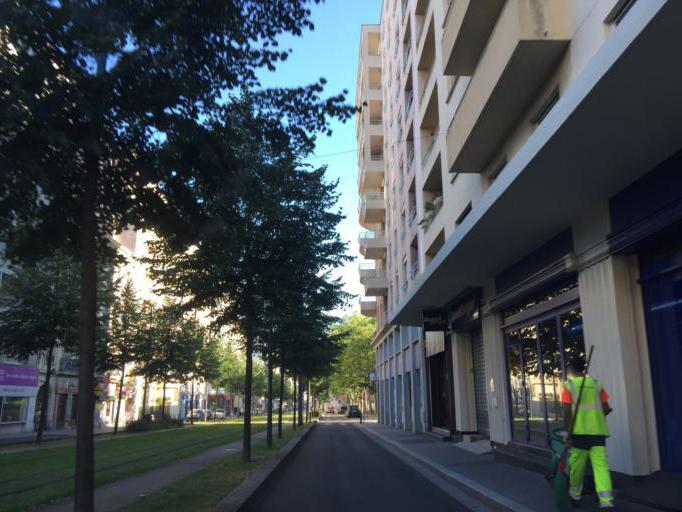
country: FR
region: Rhone-Alpes
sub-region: Departement de la Loire
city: Saint-Etienne
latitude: 45.4250
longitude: 4.3913
